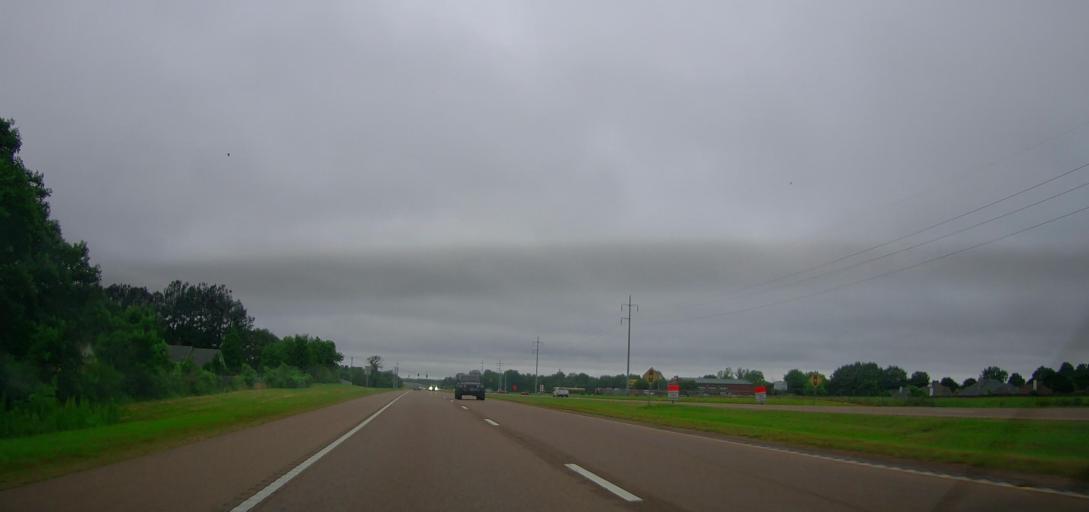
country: US
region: Mississippi
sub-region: De Soto County
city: Olive Branch
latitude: 34.9691
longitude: -89.8096
